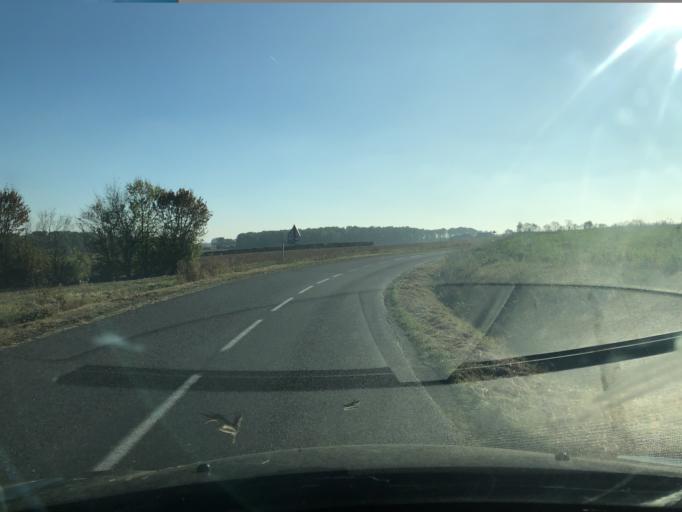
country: FR
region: Centre
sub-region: Departement d'Indre-et-Loire
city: Neuvy-le-Roi
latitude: 47.5811
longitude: 0.5996
